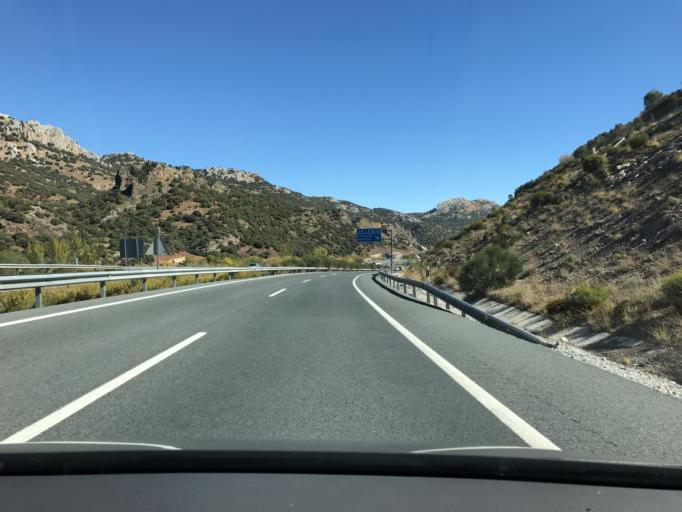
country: ES
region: Andalusia
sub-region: Provincia de Granada
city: Diezma
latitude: 37.3078
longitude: -3.4175
